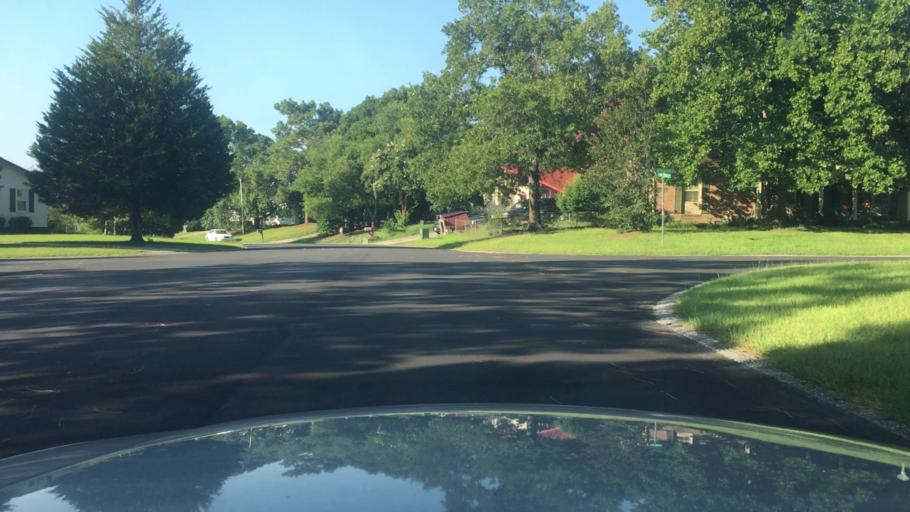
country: US
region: North Carolina
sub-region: Cumberland County
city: Spring Lake
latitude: 35.1584
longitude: -78.9053
